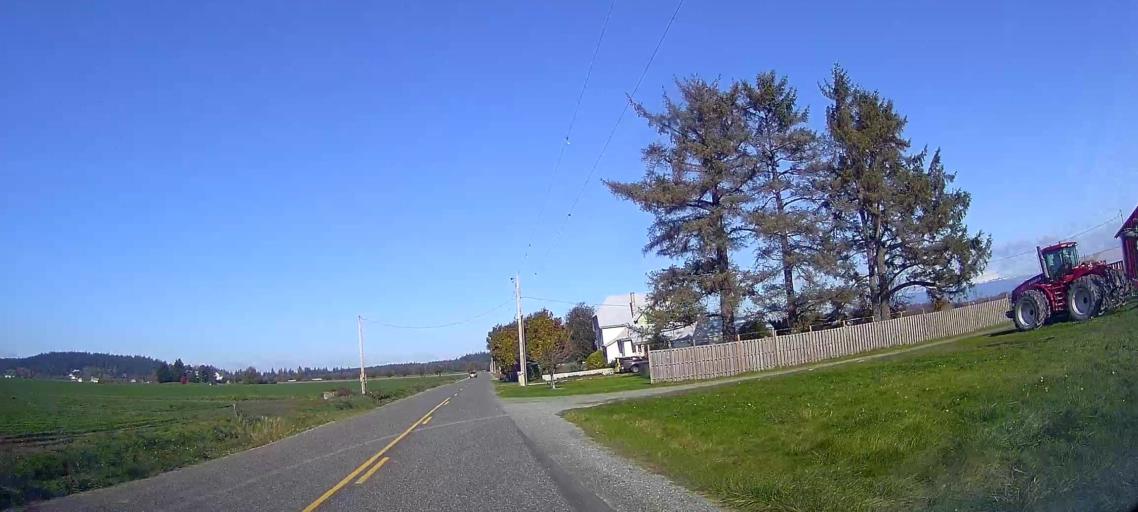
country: US
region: Washington
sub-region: Snohomish County
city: Stanwood
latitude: 48.3443
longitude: -122.4386
